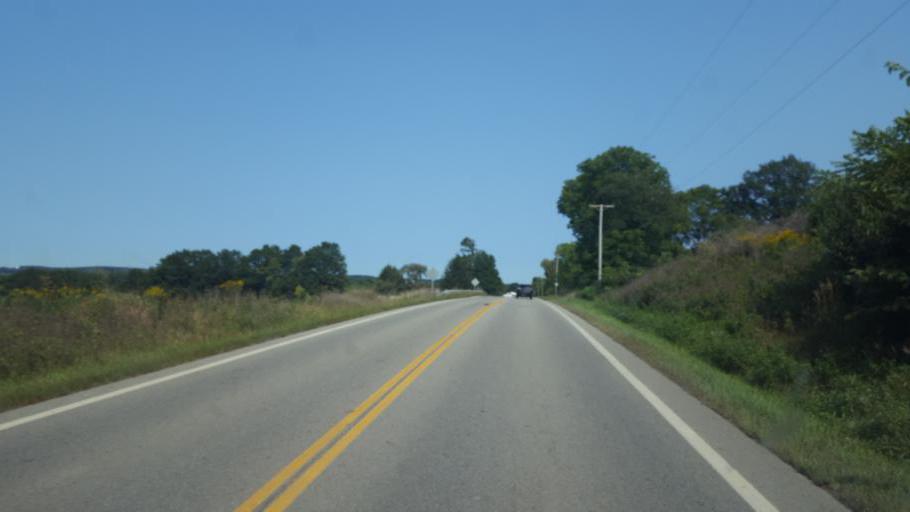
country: US
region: Ohio
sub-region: Wayne County
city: Shreve
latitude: 40.7106
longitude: -82.0845
